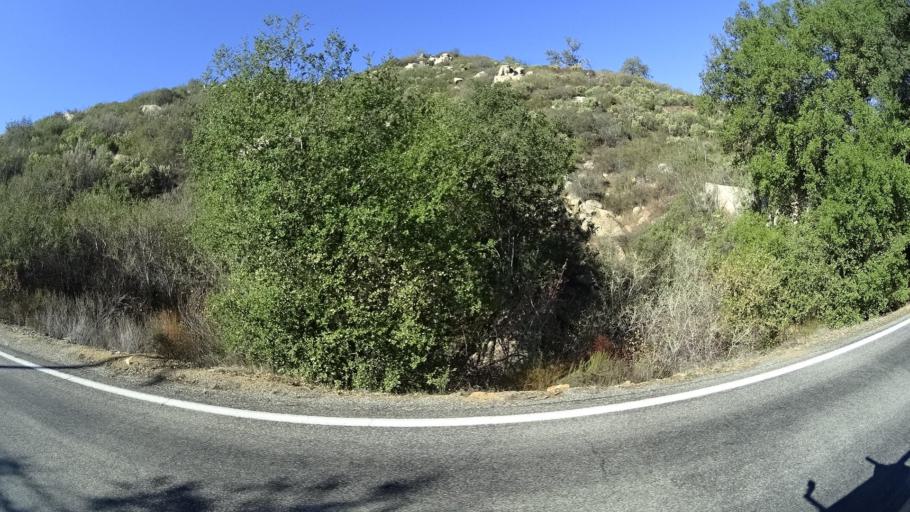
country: US
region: California
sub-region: San Diego County
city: Jamul
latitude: 32.7057
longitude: -116.7478
